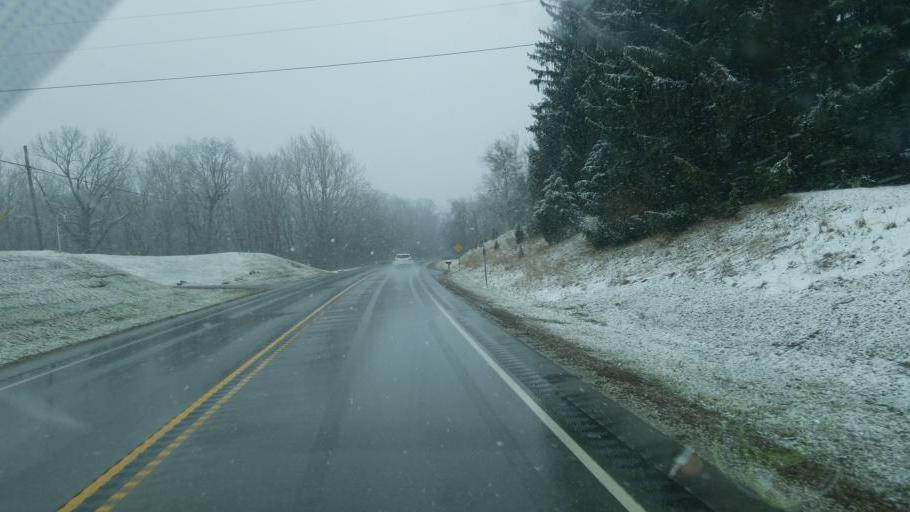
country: US
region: Indiana
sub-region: Grant County
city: Marion
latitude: 40.6162
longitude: -85.6951
